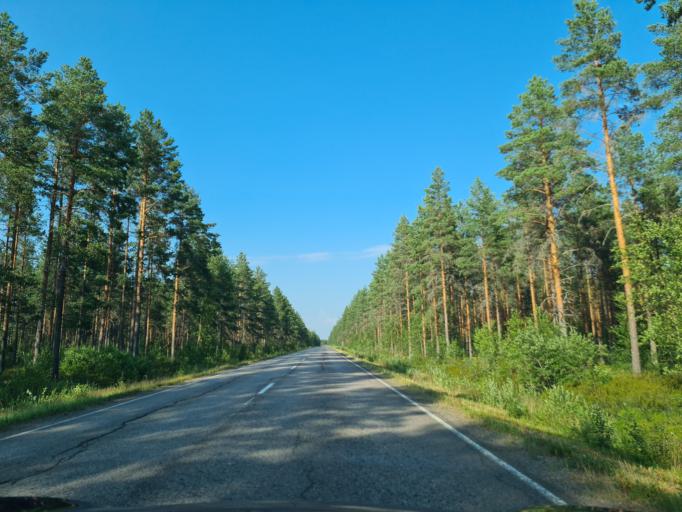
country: FI
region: Satakunta
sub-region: Pohjois-Satakunta
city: Karvia
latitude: 62.3038
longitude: 22.6399
